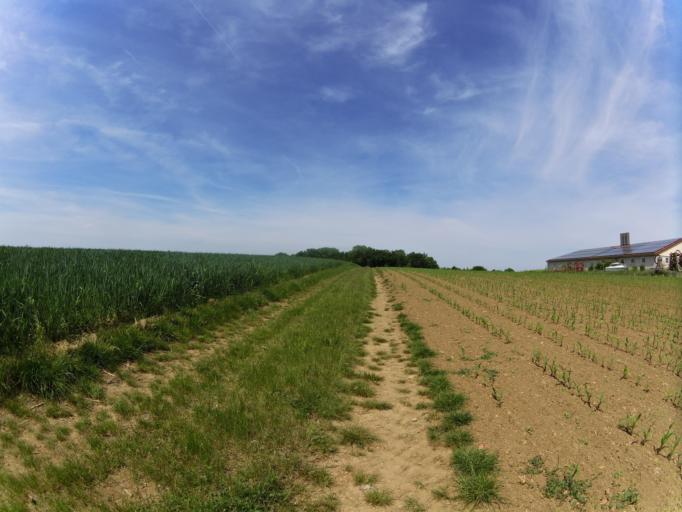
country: DE
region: Bavaria
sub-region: Regierungsbezirk Unterfranken
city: Sommerhausen
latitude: 49.6685
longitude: 10.0199
